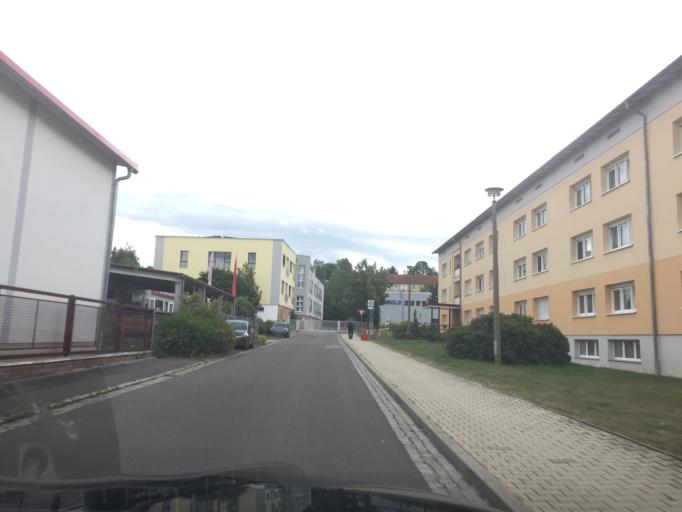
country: DE
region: Thuringia
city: Schmolln
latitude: 50.8919
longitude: 12.3457
